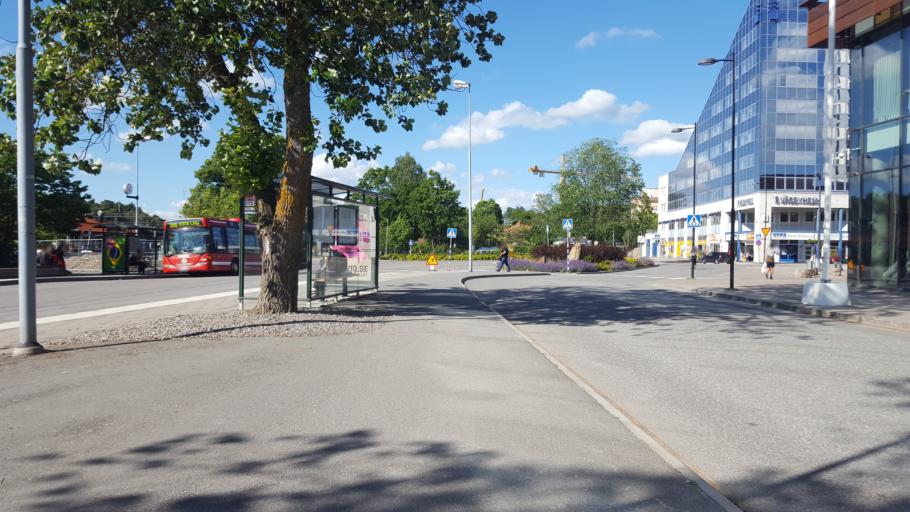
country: SE
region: Stockholm
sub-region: Upplands Vasby Kommun
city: Upplands Vaesby
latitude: 59.5209
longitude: 17.9007
